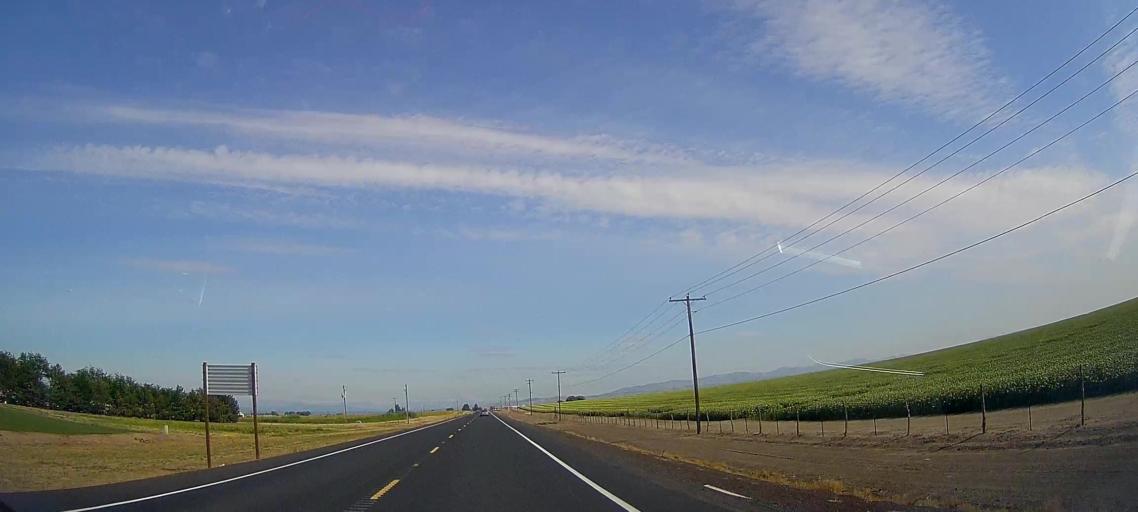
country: US
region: Oregon
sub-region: Jefferson County
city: Madras
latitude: 44.6808
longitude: -121.1476
